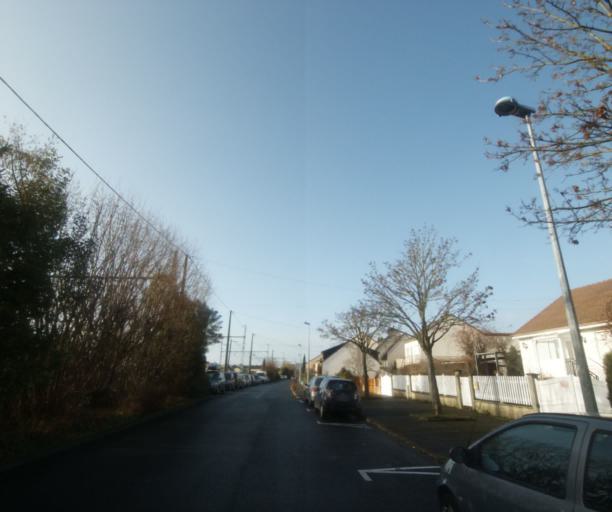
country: FR
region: Pays de la Loire
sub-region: Departement de la Sarthe
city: Le Mans
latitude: 47.9930
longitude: 0.2155
